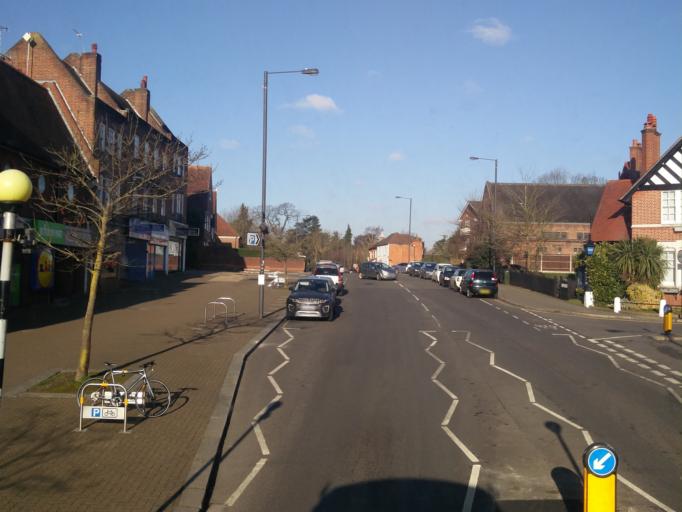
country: GB
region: England
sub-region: Greater London
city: Pinner
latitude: 51.5955
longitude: -0.3847
